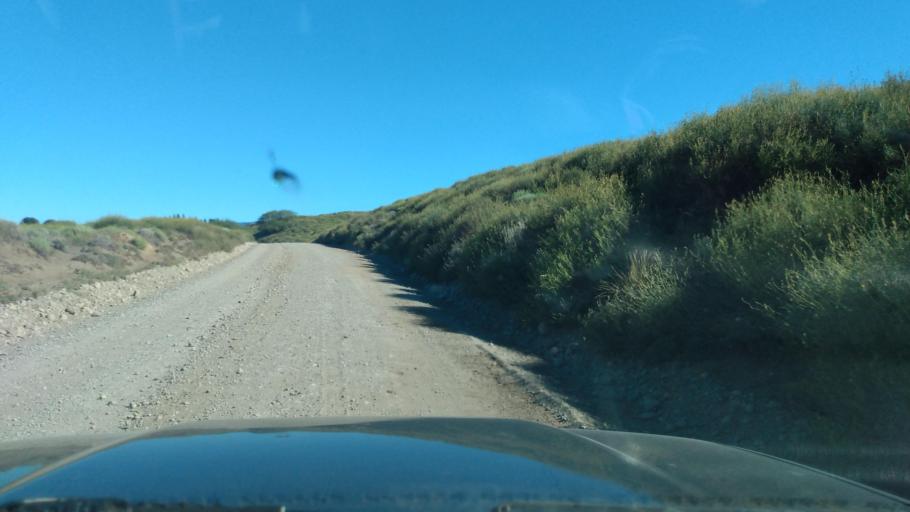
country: AR
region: Neuquen
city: Junin de los Andes
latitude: -39.8064
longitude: -71.2073
